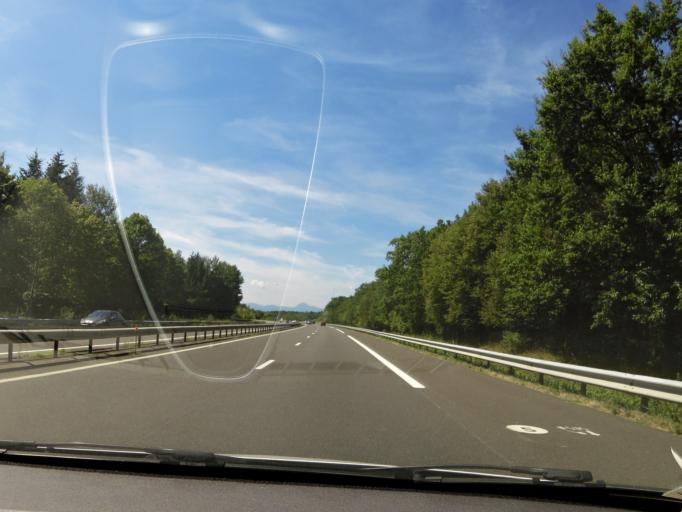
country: FR
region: Auvergne
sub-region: Departement du Puy-de-Dome
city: Lezoux
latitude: 45.8521
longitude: 3.3834
